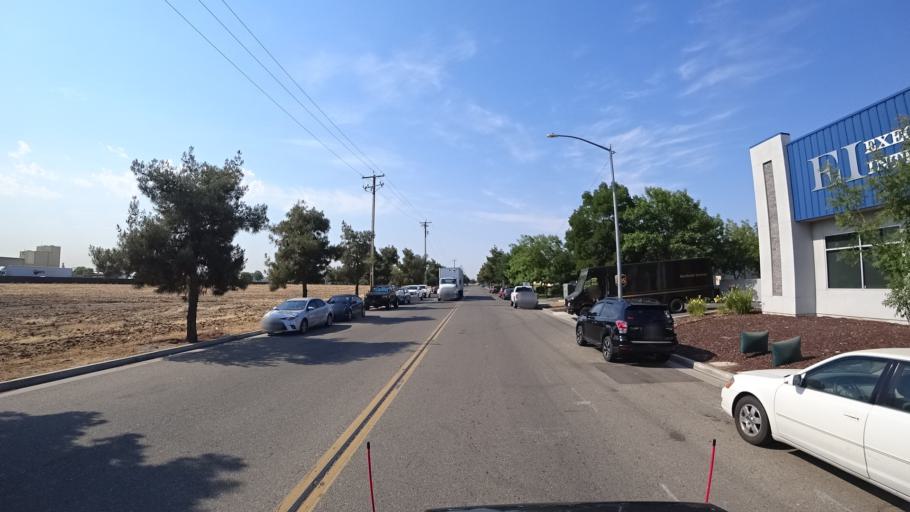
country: US
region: California
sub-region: Fresno County
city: West Park
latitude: 36.7427
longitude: -119.8267
